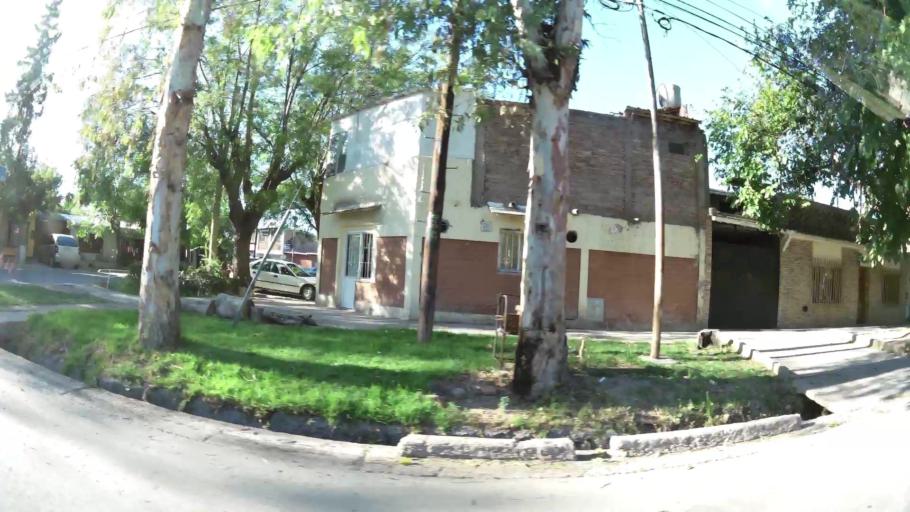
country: AR
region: Mendoza
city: Las Heras
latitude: -32.8591
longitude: -68.8240
